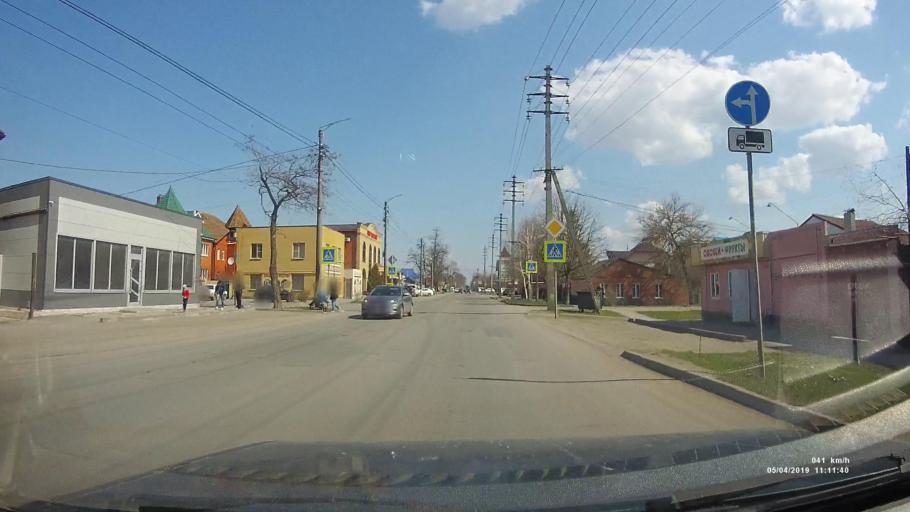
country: RU
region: Rostov
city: Azov
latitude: 47.0961
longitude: 39.4367
